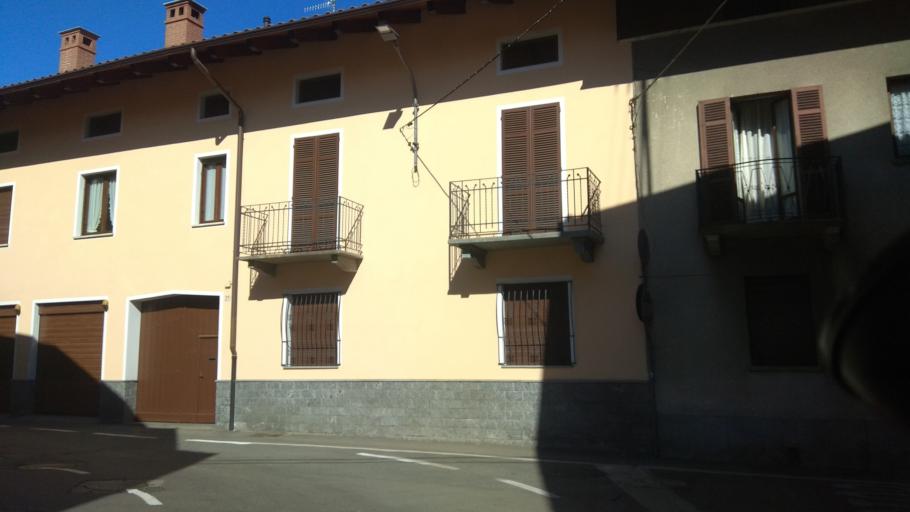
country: IT
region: Piedmont
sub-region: Provincia di Biella
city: Candelo
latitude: 45.5441
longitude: 8.1132
